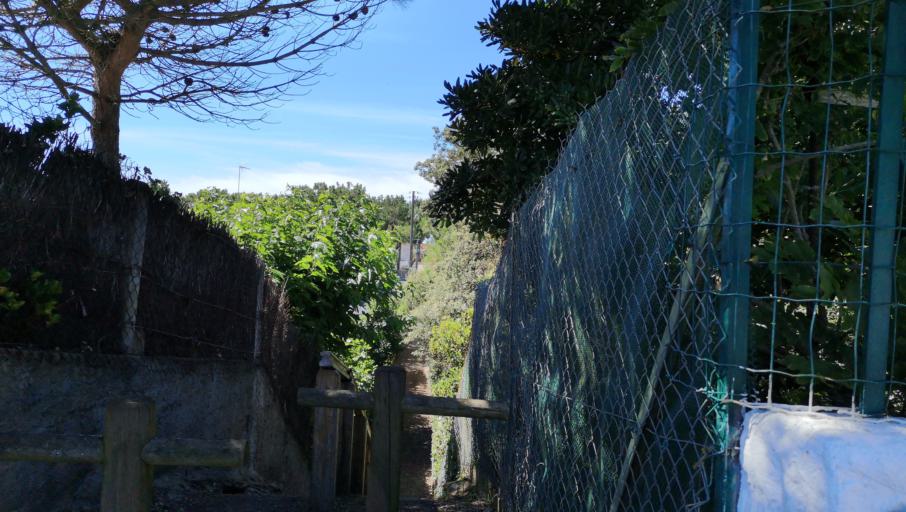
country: FR
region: Pays de la Loire
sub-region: Departement de la Vendee
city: Chateau-d'Olonne
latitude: 46.4780
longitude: -1.7573
